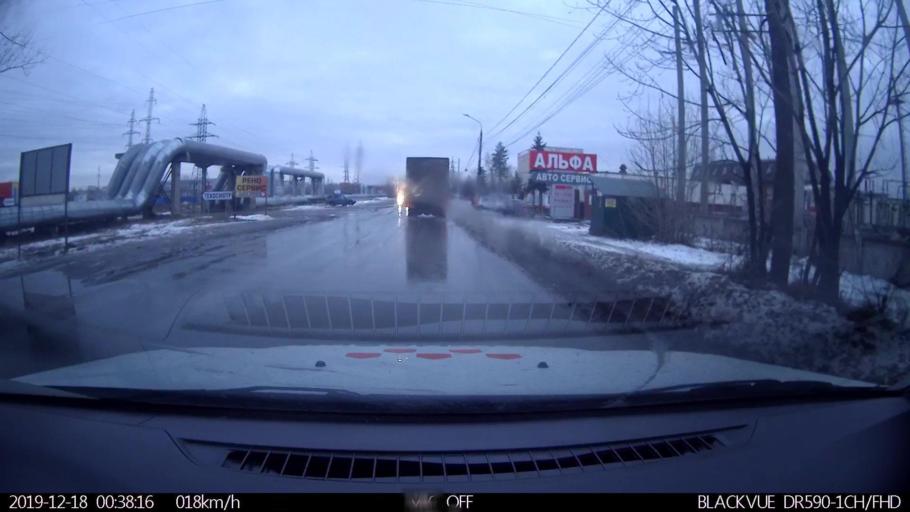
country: RU
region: Nizjnij Novgorod
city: Neklyudovo
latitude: 56.3474
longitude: 43.8918
